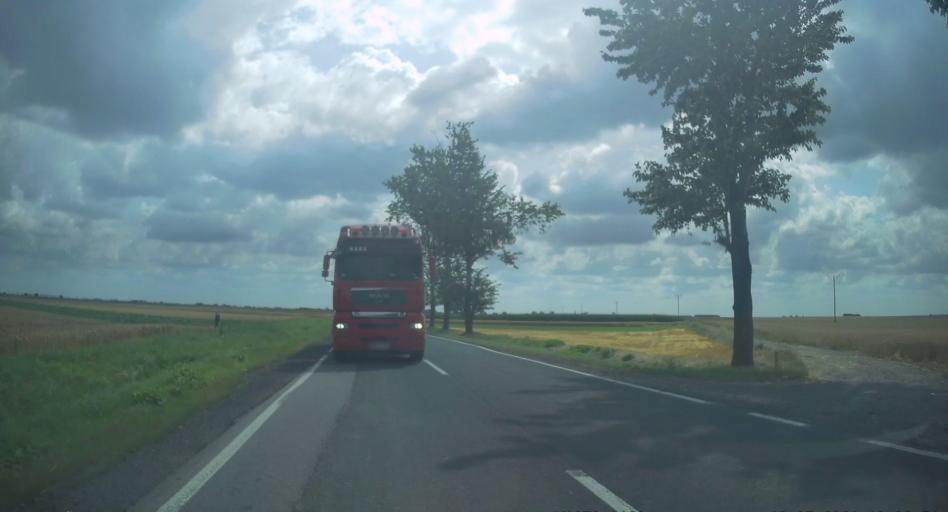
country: PL
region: Opole Voivodeship
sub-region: Powiat prudnicki
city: Glogowek
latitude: 50.3472
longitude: 17.8857
